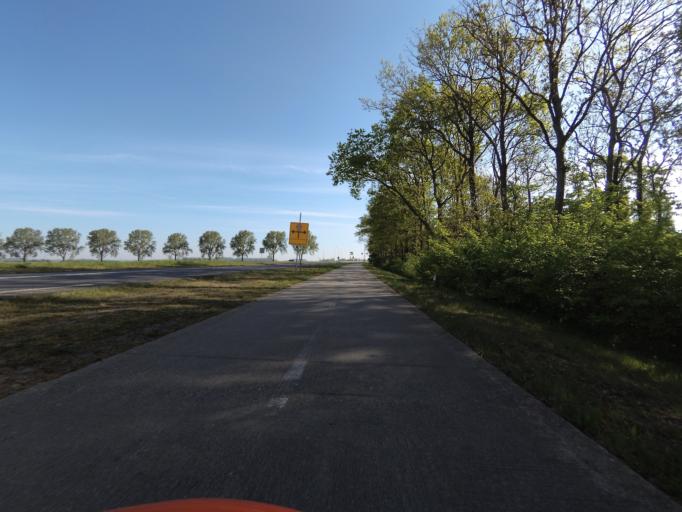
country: NL
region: Gelderland
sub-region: Gemeente Elburg
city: Elburg
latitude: 52.4571
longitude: 5.8116
